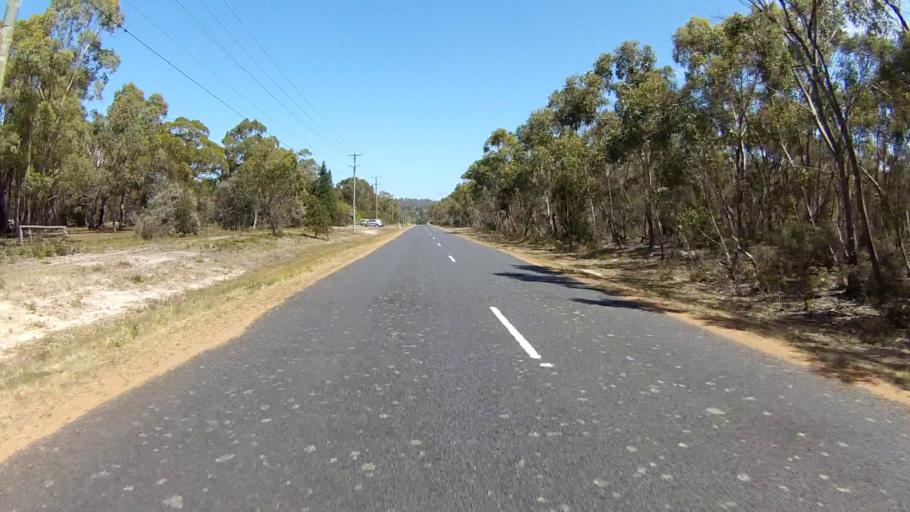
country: AU
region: Tasmania
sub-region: Clarence
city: Sandford
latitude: -42.9838
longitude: 147.4834
